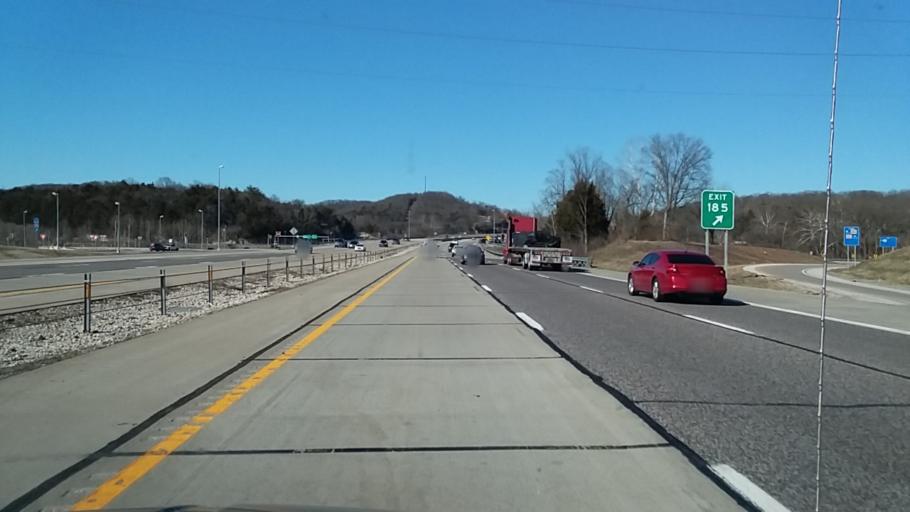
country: US
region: Missouri
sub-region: Jefferson County
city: Barnhart
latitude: 38.3447
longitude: -90.3968
